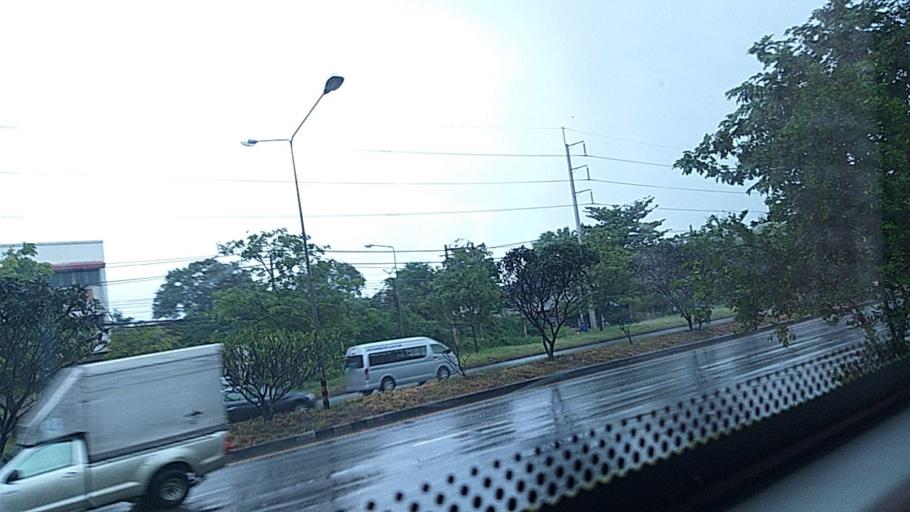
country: TH
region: Nakhon Ratchasima
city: Sikhio
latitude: 14.8653
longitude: 101.7099
